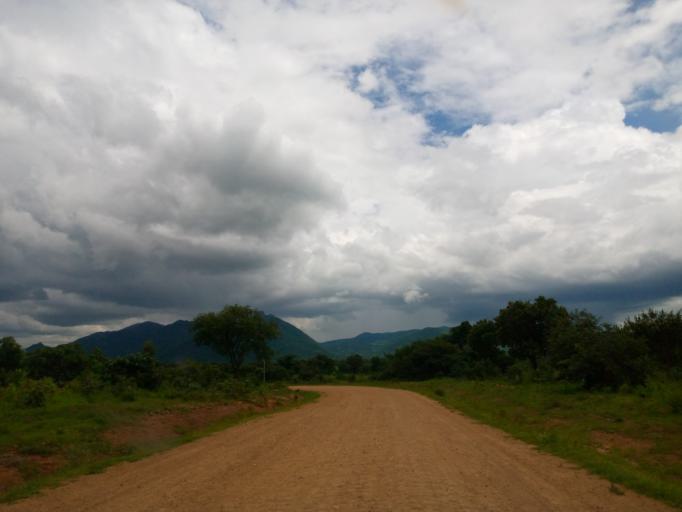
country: ET
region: Oromiya
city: Mendi
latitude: 10.1990
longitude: 35.0917
